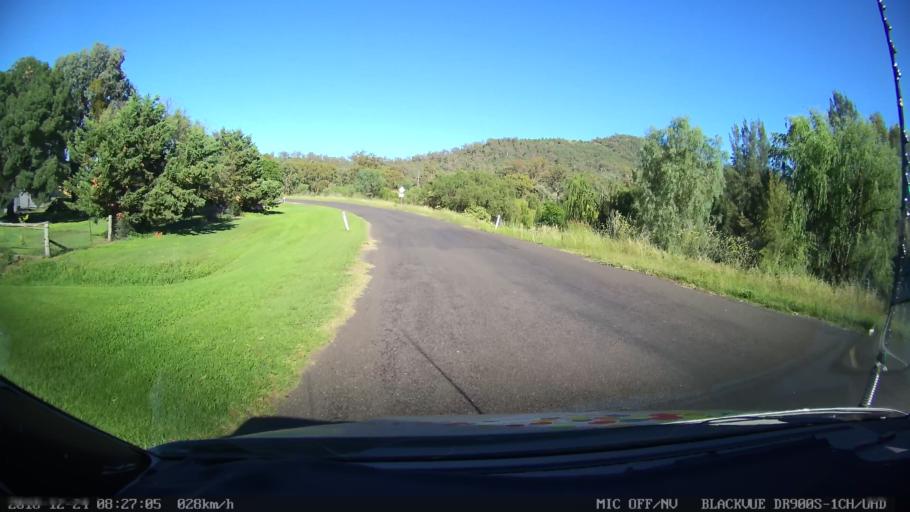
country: AU
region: New South Wales
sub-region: Tamworth Municipality
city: Phillip
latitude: -31.2604
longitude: 150.7381
